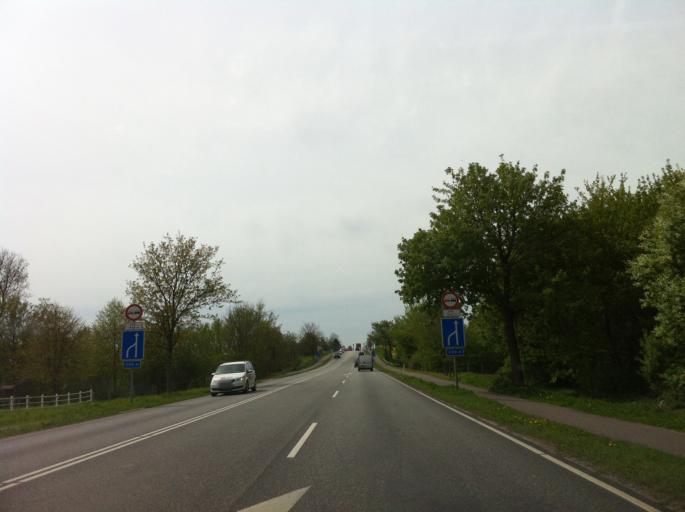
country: DK
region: Zealand
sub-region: Lejre Kommune
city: Lejre
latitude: 55.5893
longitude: 12.0060
